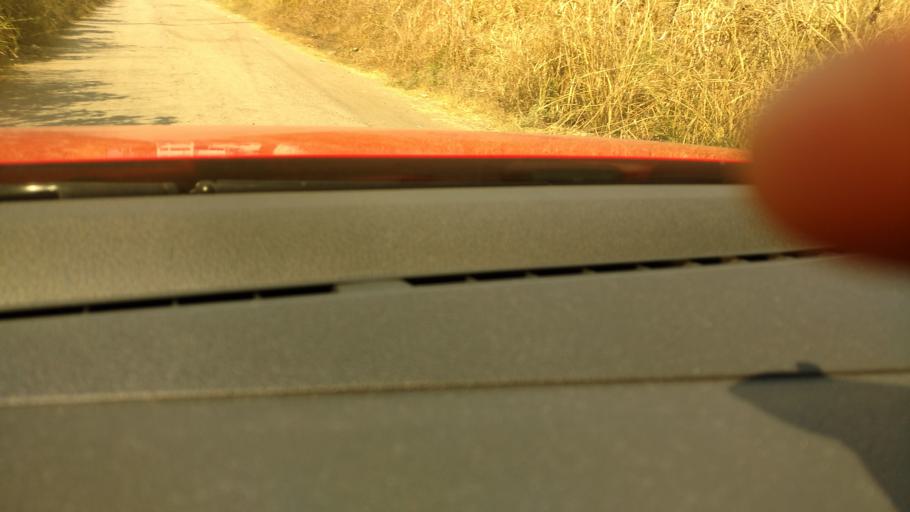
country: MX
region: Morelos
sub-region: Xochitepec
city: Chiconcuac
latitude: 18.8003
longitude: -99.2165
